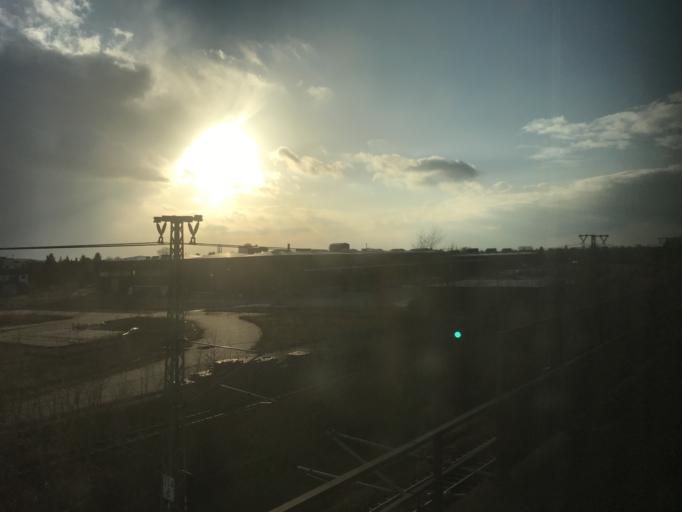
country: DE
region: Berlin
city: Falkenhagener Feld
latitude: 52.5387
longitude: 13.1719
